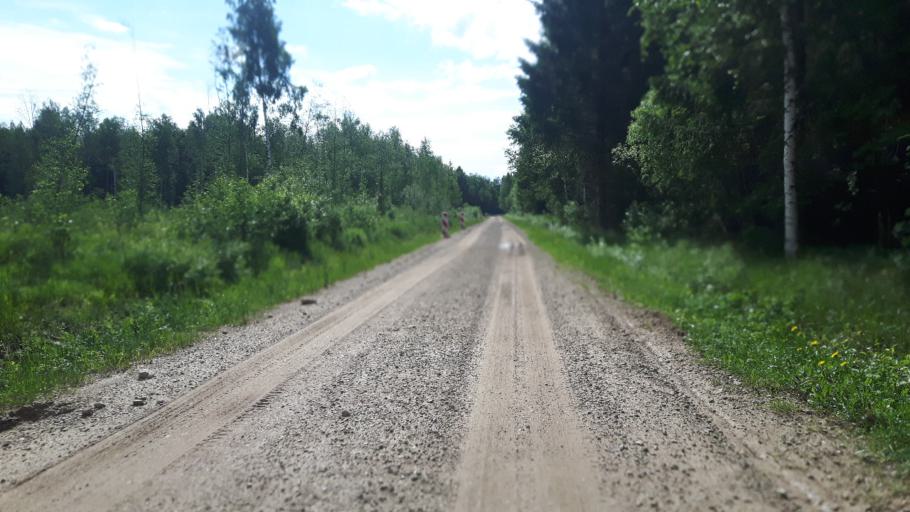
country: EE
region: Paernumaa
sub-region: Vaendra vald (alev)
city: Vandra
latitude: 58.7316
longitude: 25.0074
